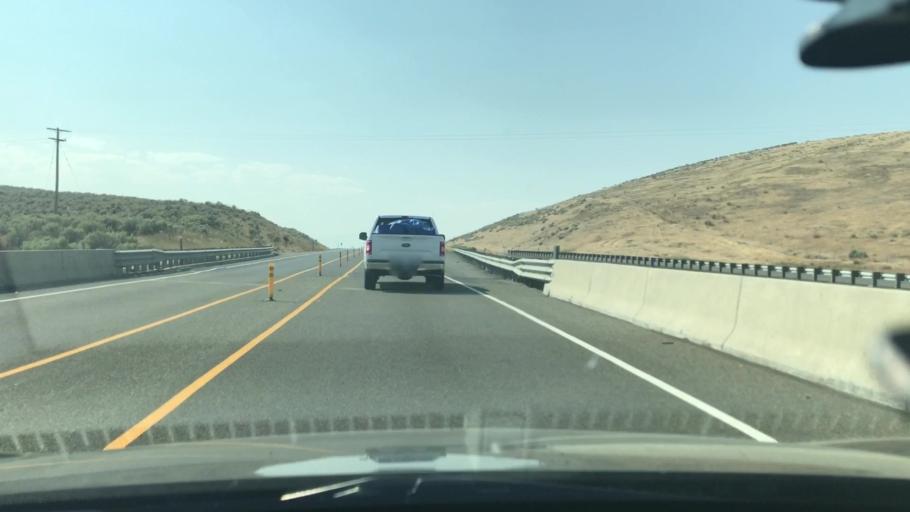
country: US
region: Oregon
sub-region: Baker County
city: Baker City
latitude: 44.6828
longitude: -117.6596
